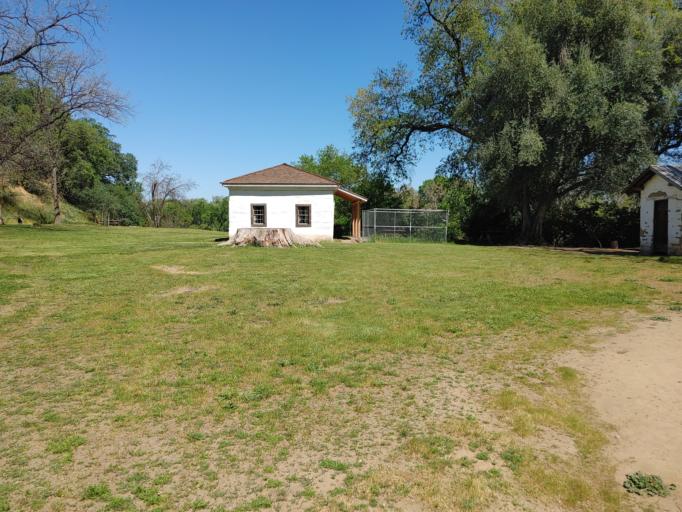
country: US
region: California
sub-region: Tehama County
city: Red Bluff
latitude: 40.1966
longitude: -122.2255
